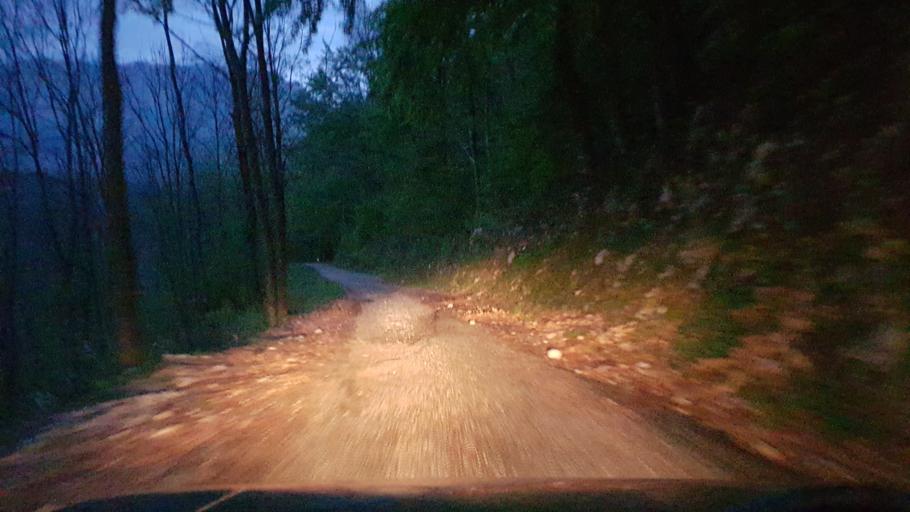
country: IT
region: Friuli Venezia Giulia
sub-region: Provincia di Udine
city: Taipana
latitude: 46.2478
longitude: 13.3562
